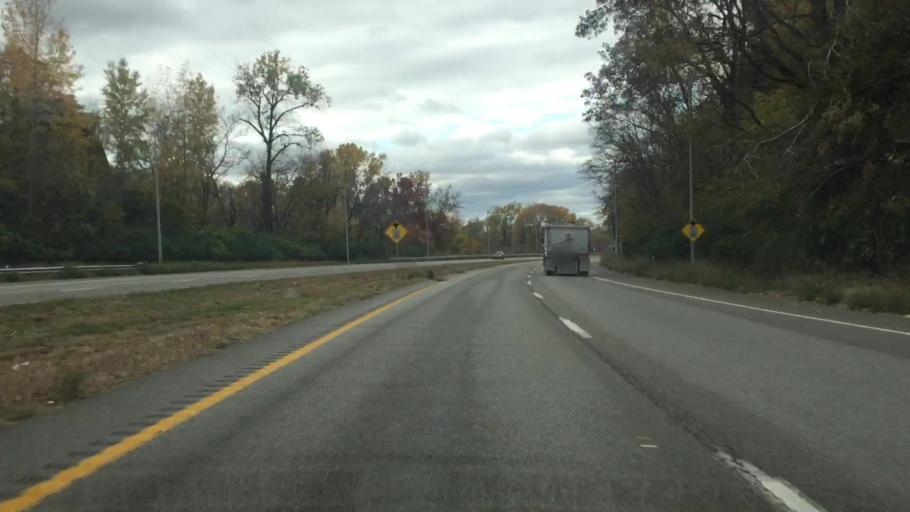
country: US
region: Missouri
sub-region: Clay County
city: North Kansas City
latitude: 39.1482
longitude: -94.5407
